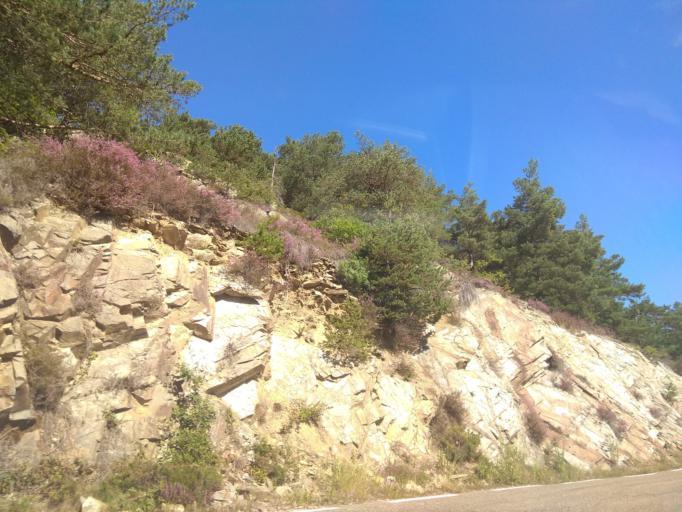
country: ES
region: Catalonia
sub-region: Provincia de Lleida
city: Vielha
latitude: 42.7400
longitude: 0.7466
